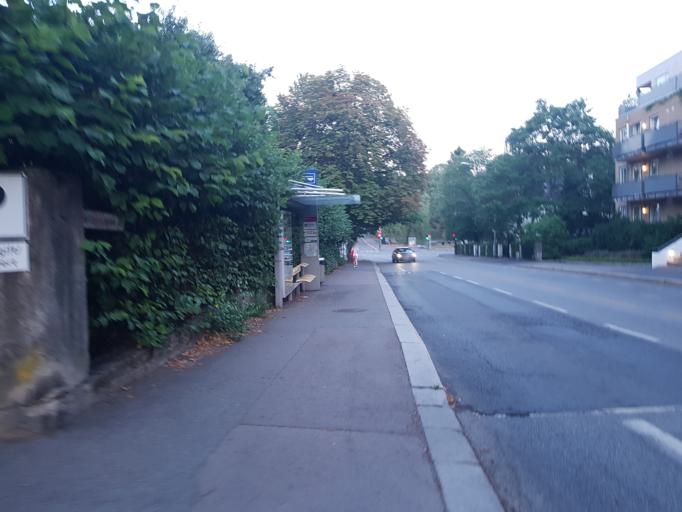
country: NO
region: Oslo
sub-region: Oslo
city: Oslo
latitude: 59.9308
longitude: 10.7429
